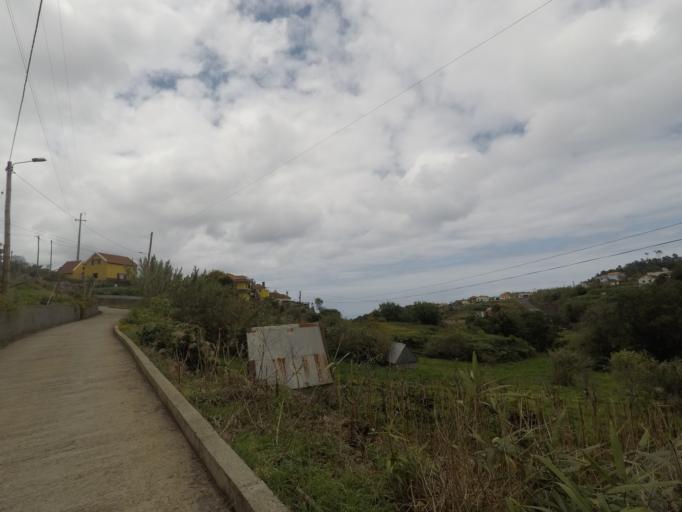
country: PT
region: Madeira
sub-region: Santana
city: Santana
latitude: 32.8025
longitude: -16.8733
